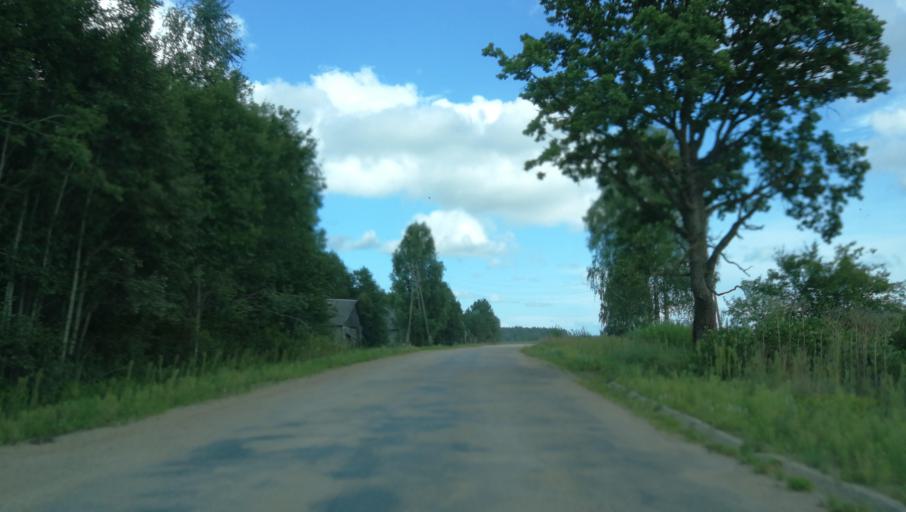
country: LV
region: Malpils
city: Malpils
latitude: 56.9621
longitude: 24.9307
